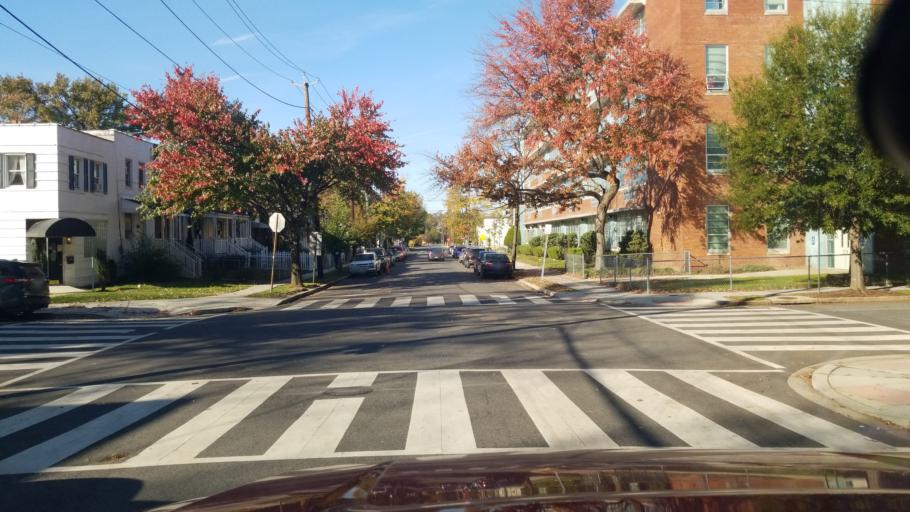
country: US
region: Maryland
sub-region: Prince George's County
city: Fairmount Heights
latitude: 38.8958
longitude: -76.9189
